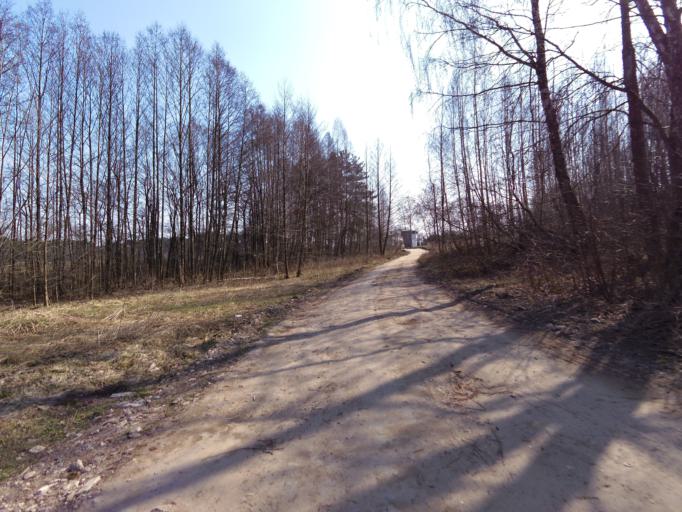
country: LT
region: Vilnius County
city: Pilaite
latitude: 54.6960
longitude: 25.1730
